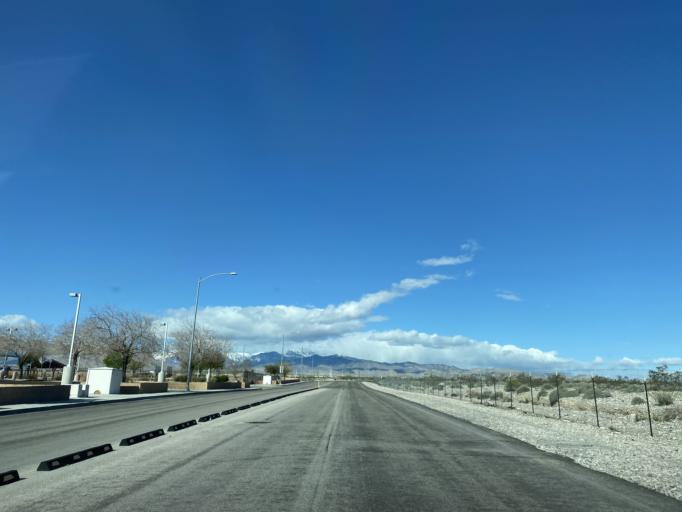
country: US
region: Nevada
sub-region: Clark County
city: Summerlin South
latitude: 36.3214
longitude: -115.2994
